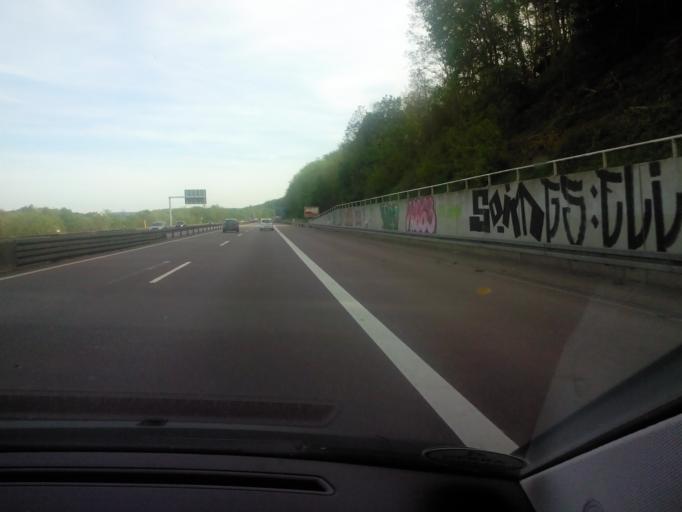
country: DE
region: Saarland
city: Wadgassen
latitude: 49.2803
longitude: 6.7698
